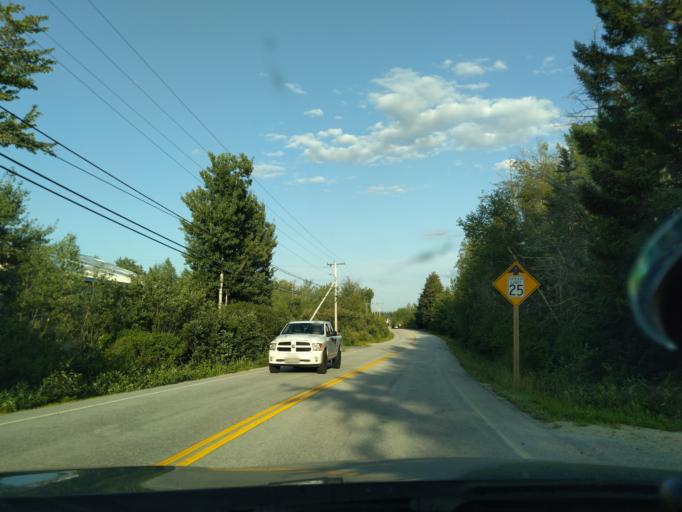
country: US
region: Maine
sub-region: Hancock County
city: Gouldsboro
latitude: 44.3914
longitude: -68.0492
